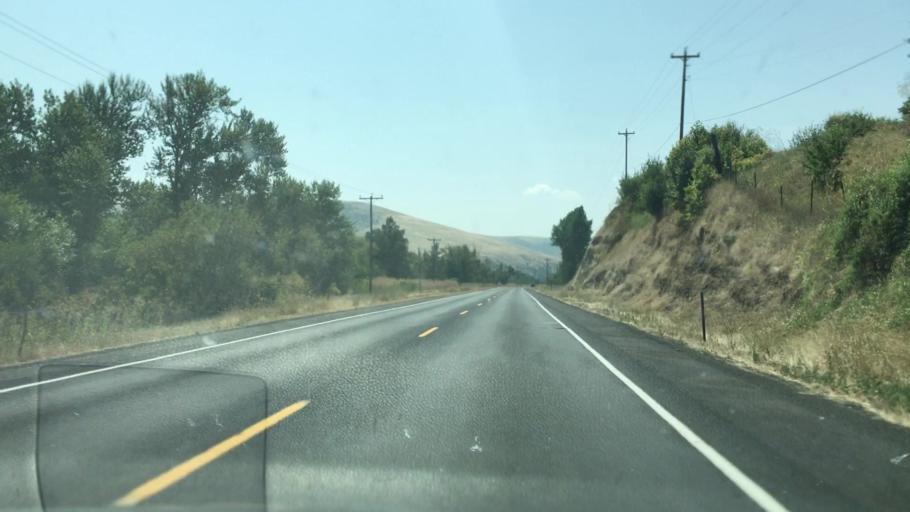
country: US
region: Idaho
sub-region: Nez Perce County
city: Lapwai
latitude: 46.3894
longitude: -116.7976
